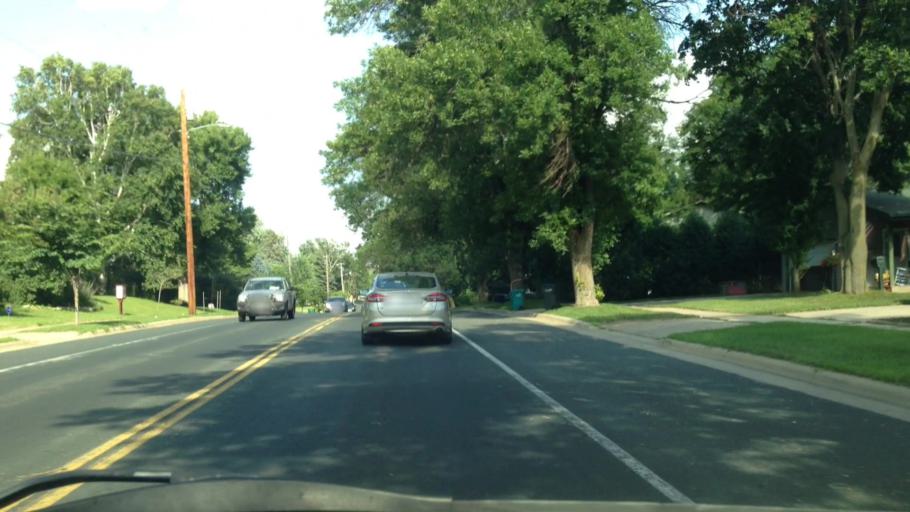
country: US
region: Minnesota
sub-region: Olmsted County
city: Rochester
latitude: 44.0435
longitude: -92.4977
